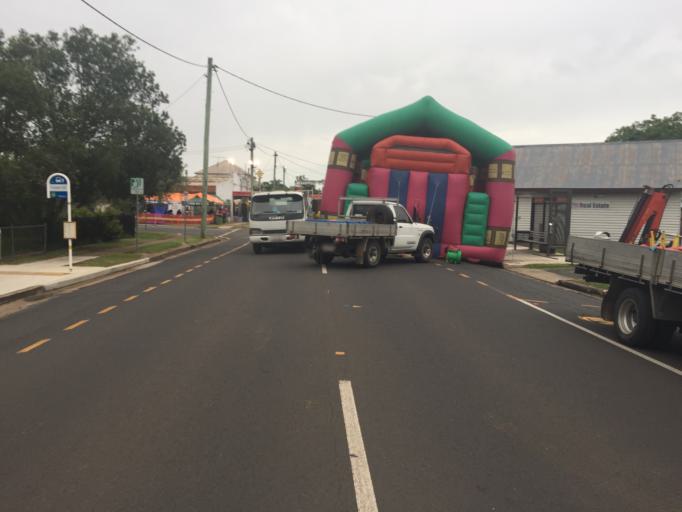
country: AU
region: Queensland
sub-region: Lockyer Valley
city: Gatton
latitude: -27.5905
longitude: 152.3565
